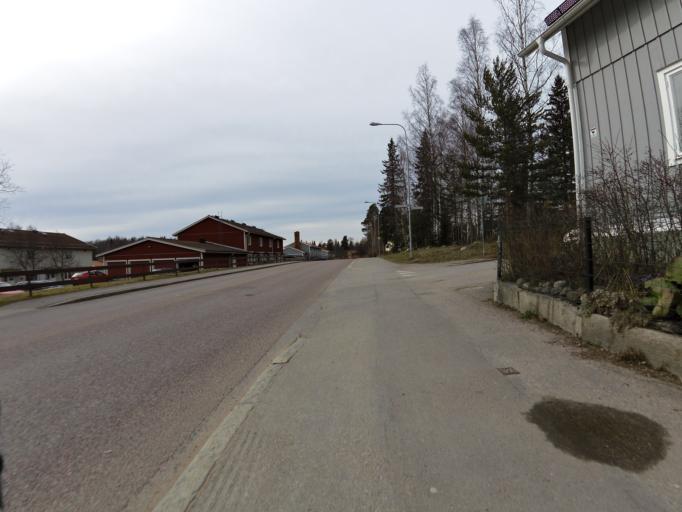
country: SE
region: Gaevleborg
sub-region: Hofors Kommun
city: Hofors
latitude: 60.5465
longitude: 16.2804
